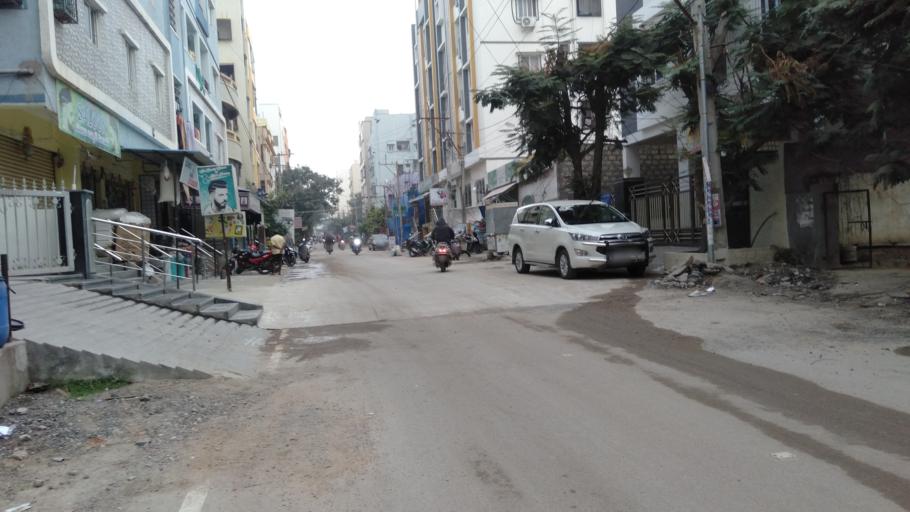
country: IN
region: Telangana
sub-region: Rangareddi
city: Kukatpalli
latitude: 17.4939
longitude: 78.3883
